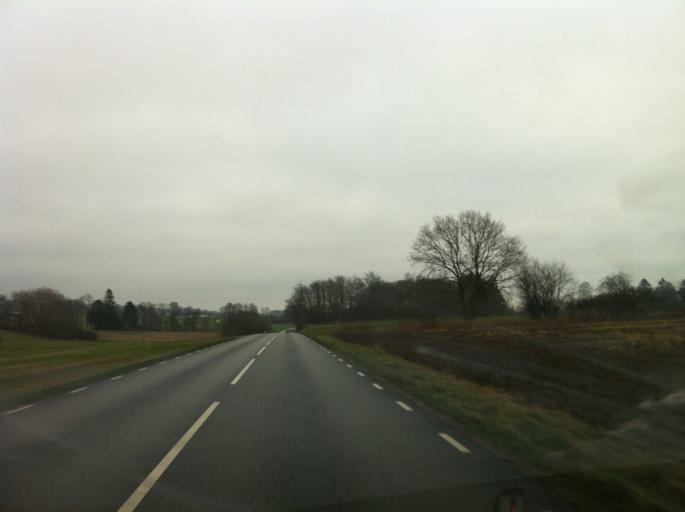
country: SE
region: Skane
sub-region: Hoors Kommun
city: Loberod
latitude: 55.7434
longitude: 13.4198
